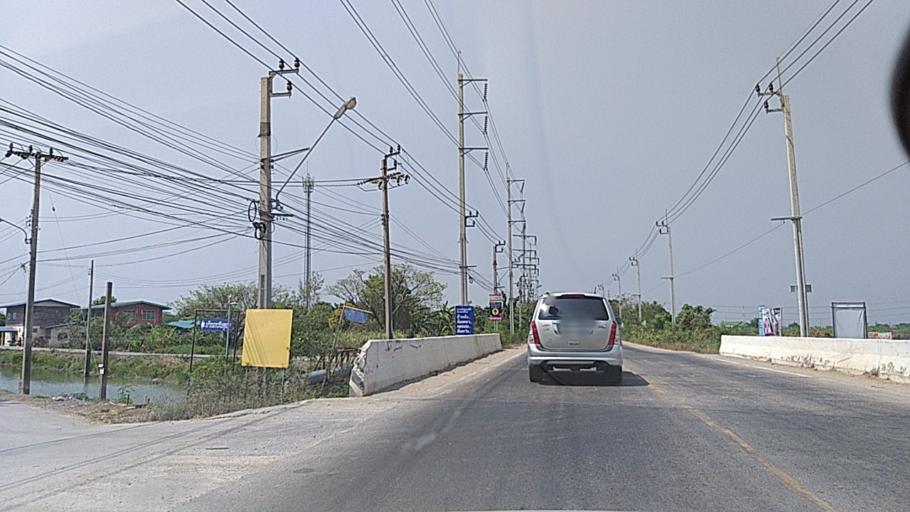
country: TH
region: Nonthaburi
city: Sai Noi
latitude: 13.9559
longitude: 100.3112
